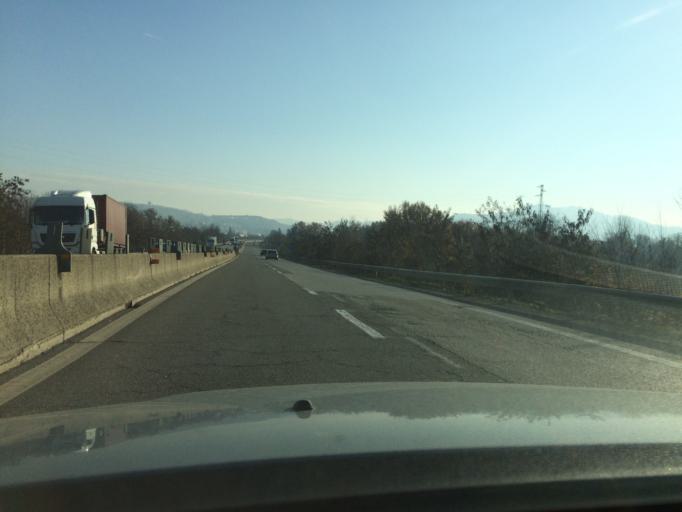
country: IT
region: Umbria
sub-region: Provincia di Perugia
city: Ponterio-Pian di Porto
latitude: 42.8180
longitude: 12.4011
